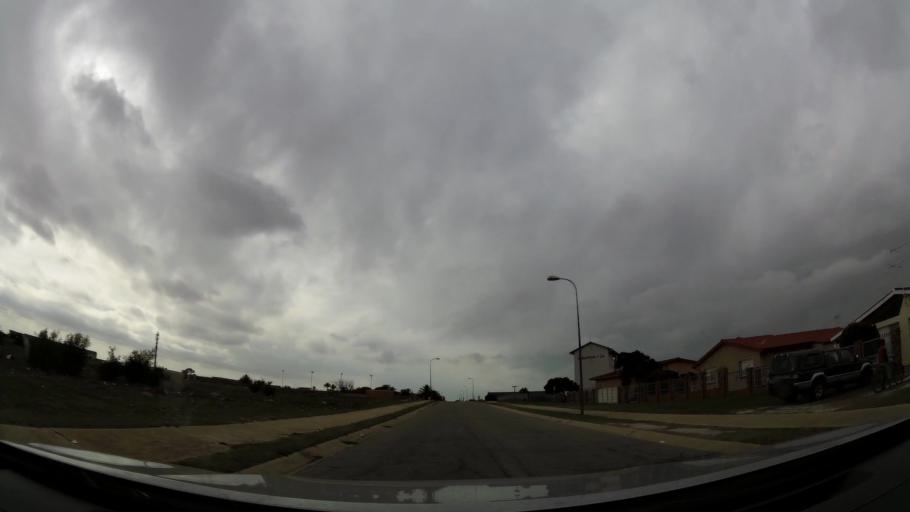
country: ZA
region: Eastern Cape
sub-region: Nelson Mandela Bay Metropolitan Municipality
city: Port Elizabeth
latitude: -33.9044
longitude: 25.5578
